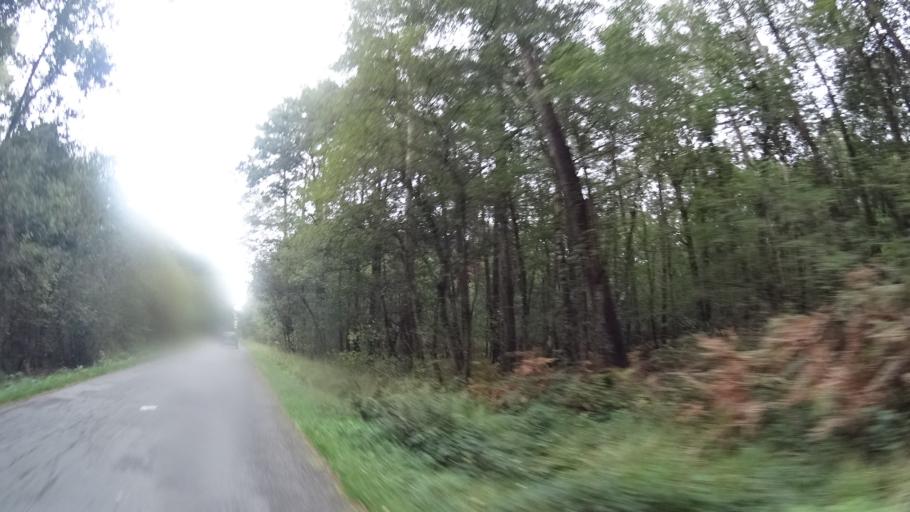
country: FR
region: Brittany
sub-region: Departement d'Ille-et-Vilaine
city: Paimpont
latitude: 48.0795
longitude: -2.1497
